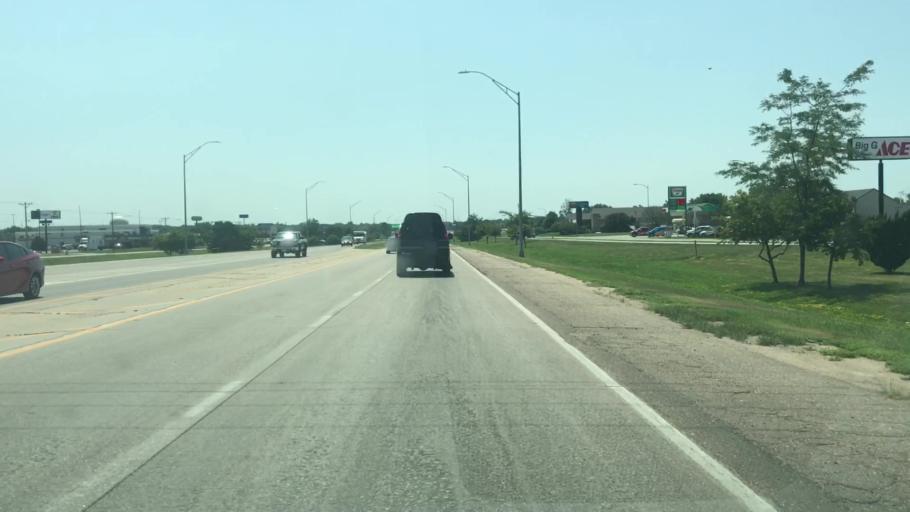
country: US
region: Nebraska
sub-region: Adams County
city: Hastings
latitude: 40.6185
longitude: -98.3831
